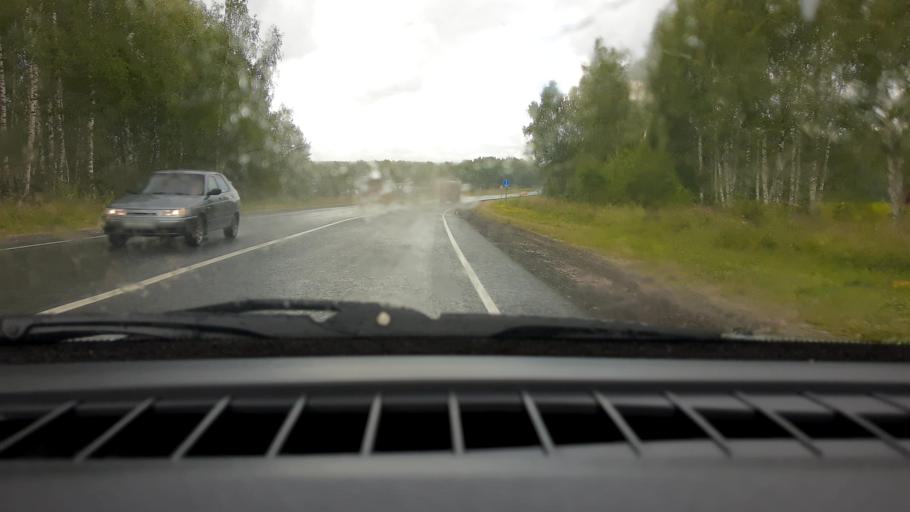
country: RU
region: Nizjnij Novgorod
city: Linda
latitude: 56.6694
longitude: 44.1398
